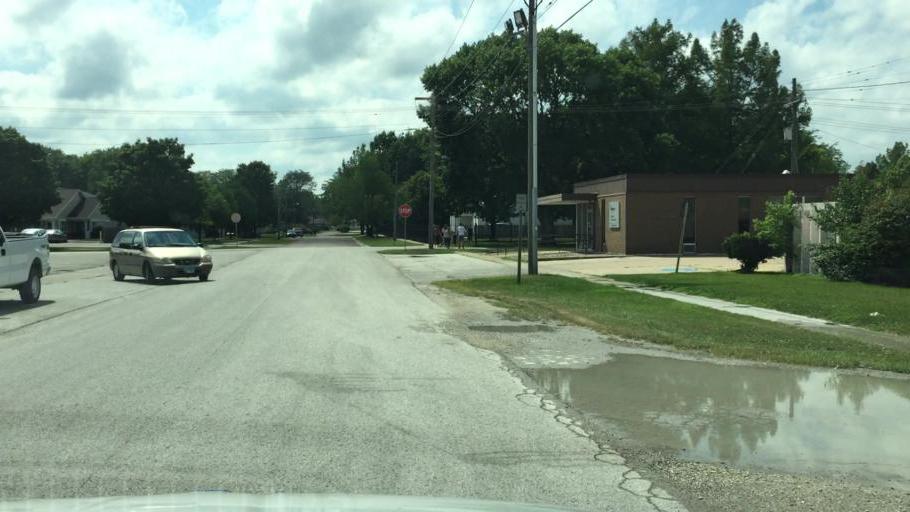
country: US
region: Illinois
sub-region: Hancock County
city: Carthage
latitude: 40.4145
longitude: -91.1380
